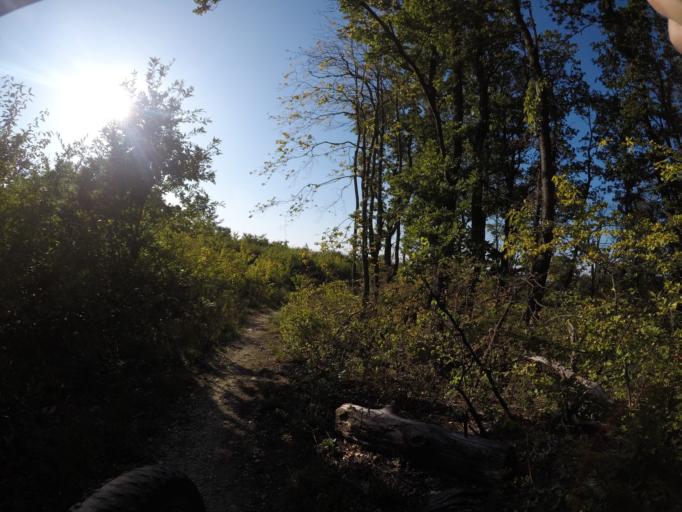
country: AT
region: Lower Austria
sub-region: Politischer Bezirk Bruck an der Leitha
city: Mannersdorf am Leithagebirge
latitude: 47.9665
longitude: 16.6153
